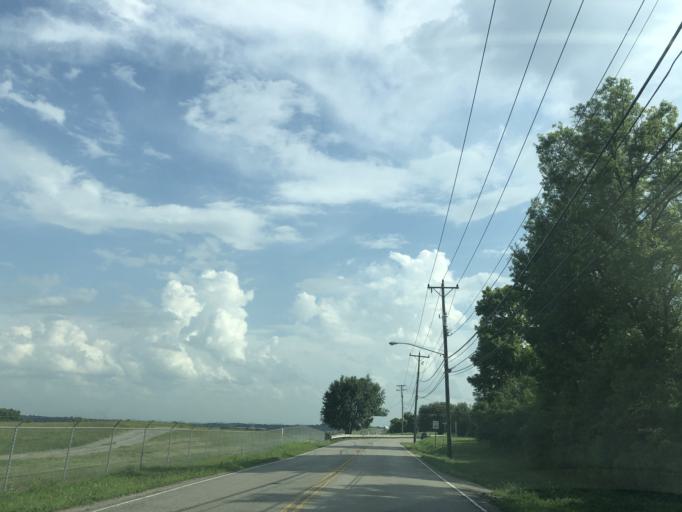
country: US
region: Tennessee
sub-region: Davidson County
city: Oak Hill
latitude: 36.1081
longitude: -86.6897
